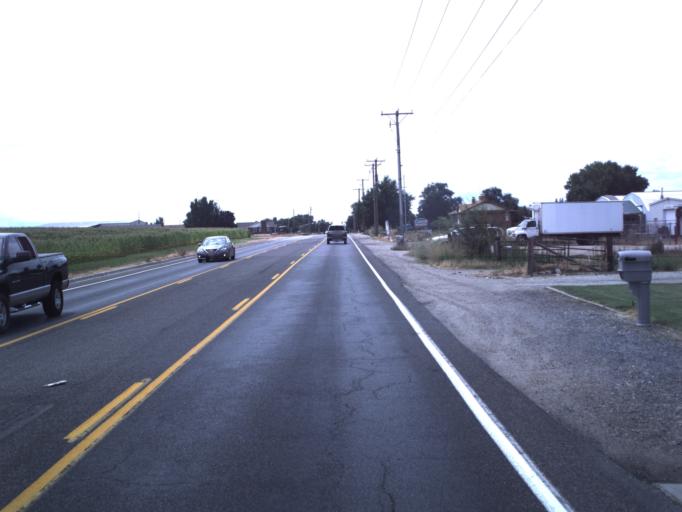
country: US
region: Utah
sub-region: Davis County
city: Clinton
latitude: 41.1302
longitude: -112.0645
